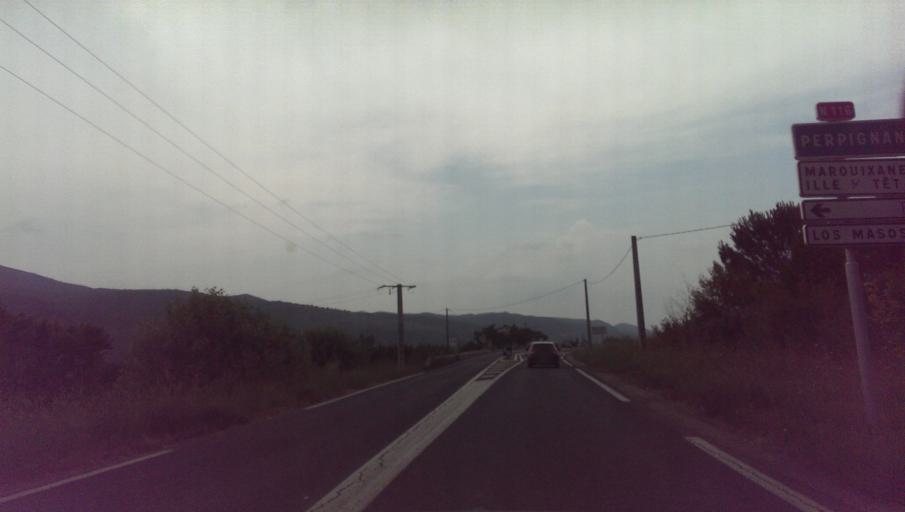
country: FR
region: Languedoc-Roussillon
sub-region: Departement des Pyrenees-Orientales
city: Prades
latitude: 42.6304
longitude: 2.4557
